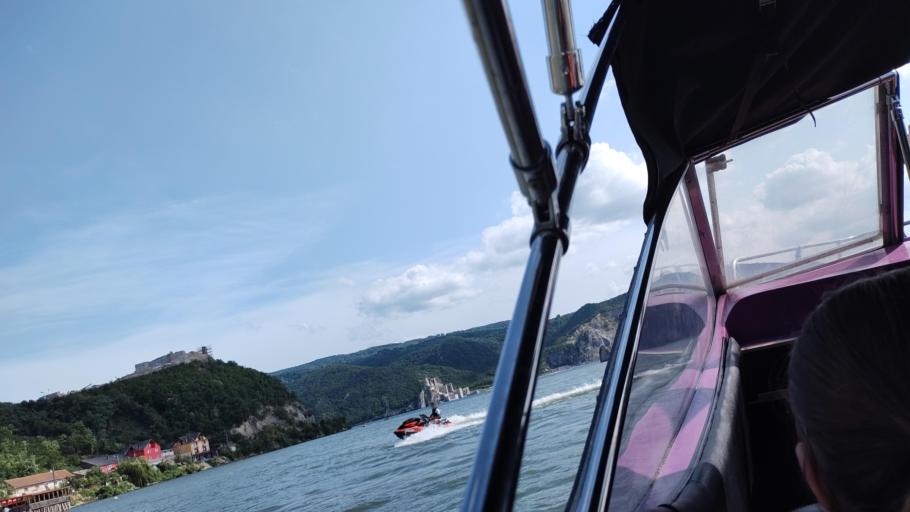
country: RO
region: Caras-Severin
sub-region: Comuna Pescari
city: Coronini
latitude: 44.6770
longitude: 21.6784
